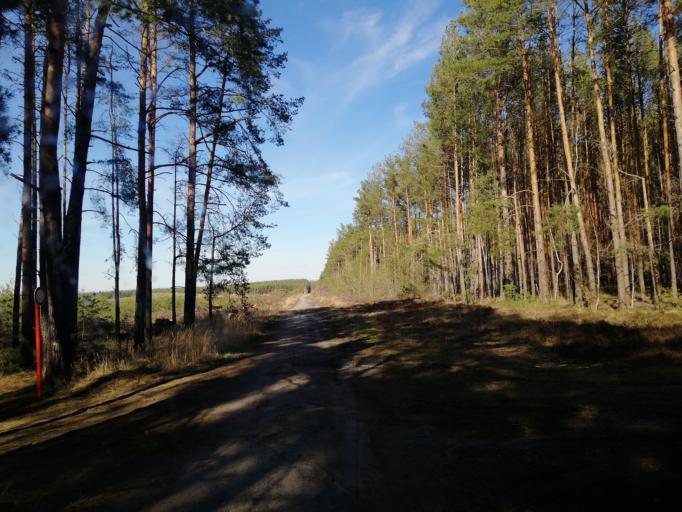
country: DE
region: Brandenburg
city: Ruckersdorf
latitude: 51.5697
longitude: 13.5943
